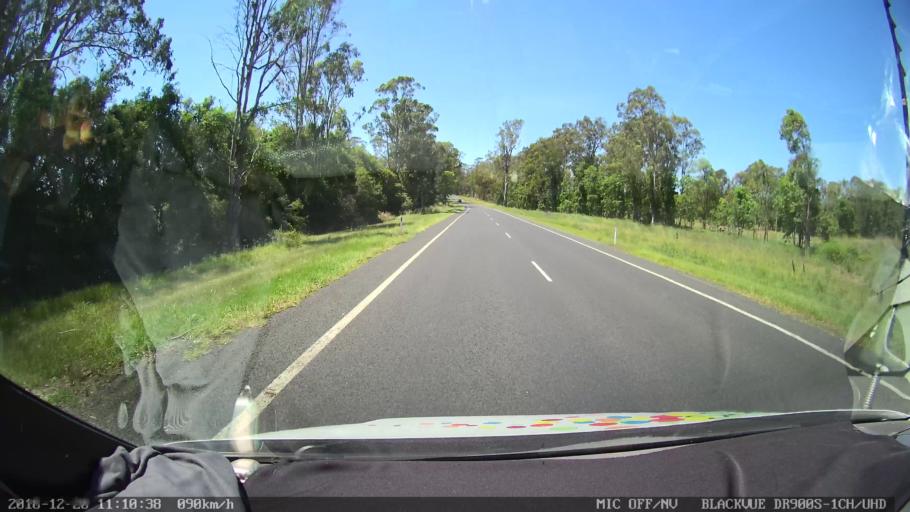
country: AU
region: New South Wales
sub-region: Richmond Valley
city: Casino
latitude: -28.9516
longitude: 153.0098
